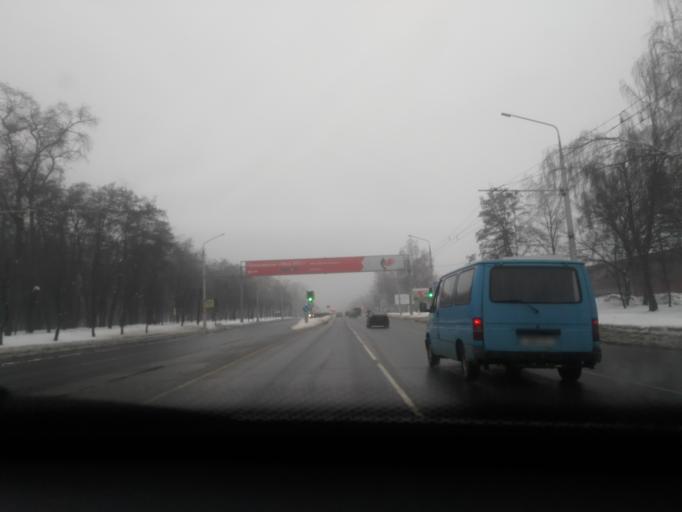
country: BY
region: Mogilev
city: Babruysk
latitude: 53.1674
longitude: 29.2074
